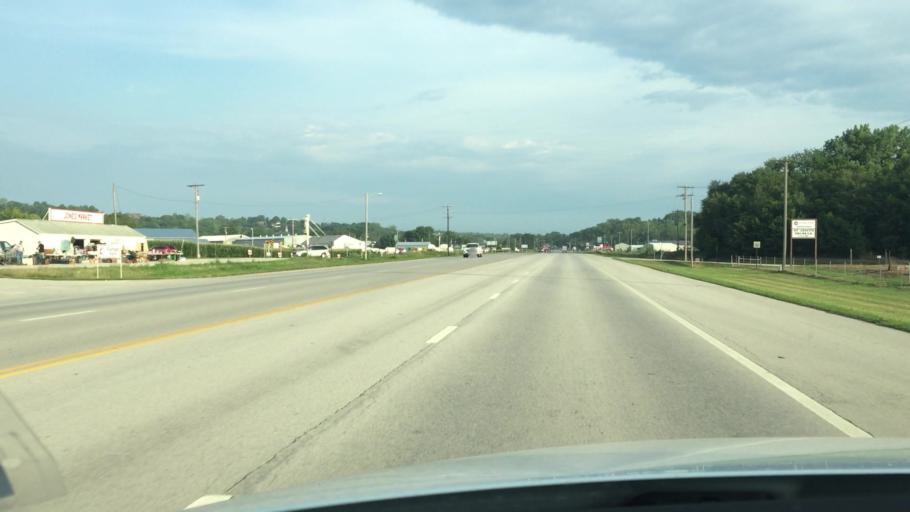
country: US
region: Kansas
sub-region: Doniphan County
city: Wathena
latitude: 39.7537
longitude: -94.9348
